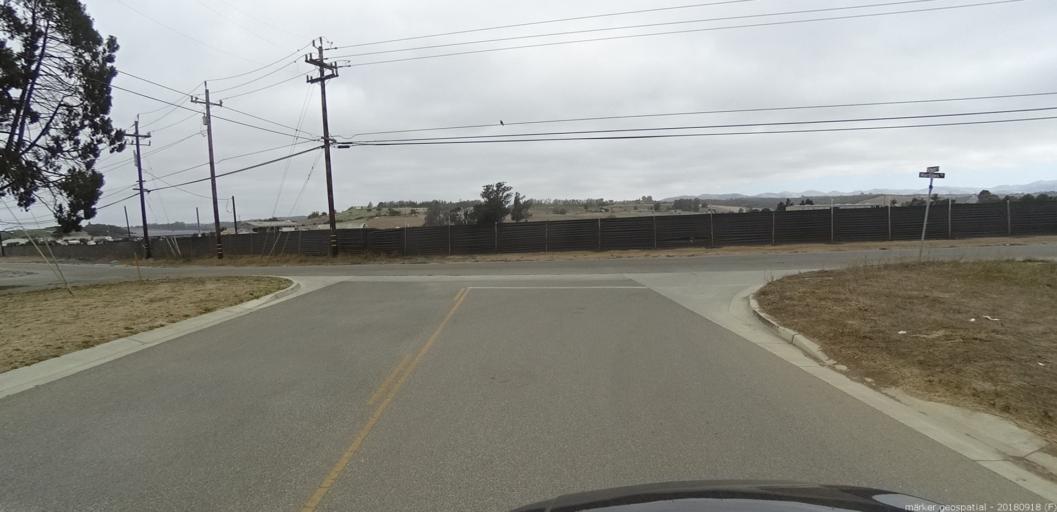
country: US
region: California
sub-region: Monterey County
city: Prunedale
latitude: 36.7501
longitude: -121.6603
